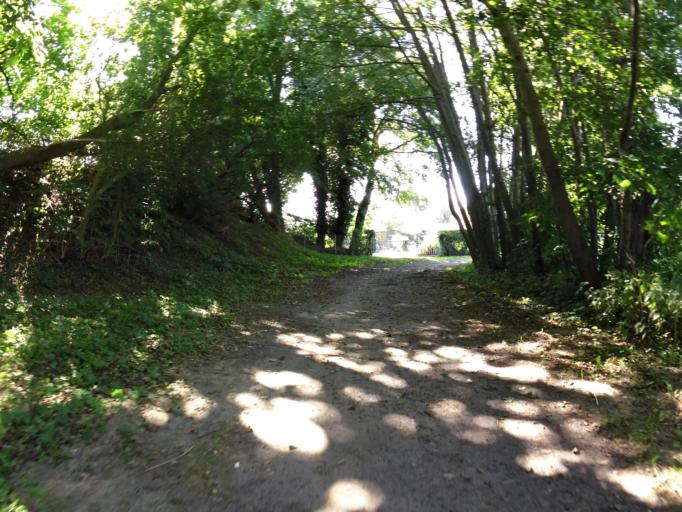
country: DE
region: Mecklenburg-Vorpommern
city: Seebad Heringsdorf
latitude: 53.9620
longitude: 14.1553
